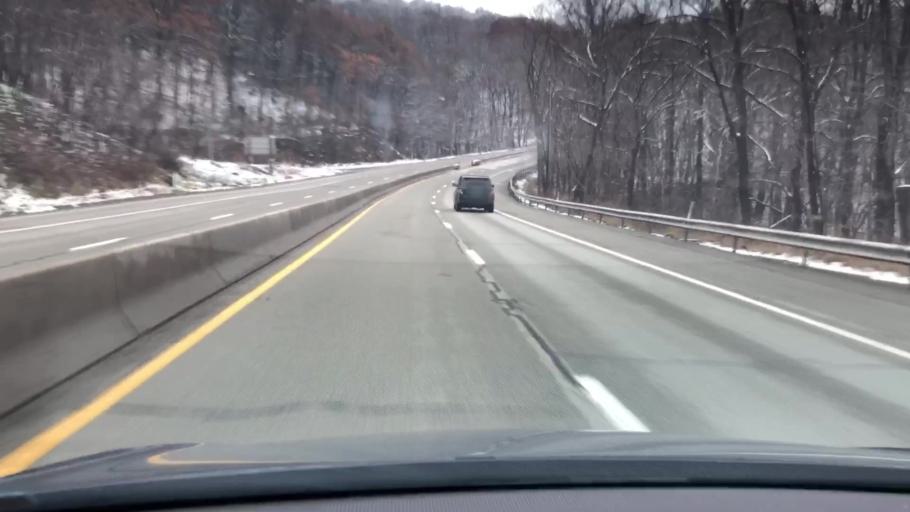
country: US
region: Pennsylvania
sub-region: Fayette County
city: Hopwood
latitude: 39.8656
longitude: -79.6823
